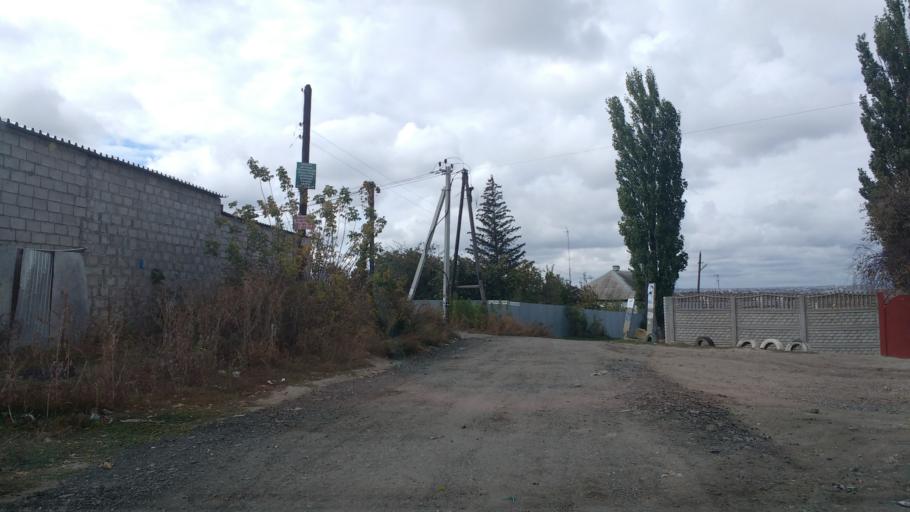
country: RU
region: Volgograd
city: Vodstroy
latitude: 48.7778
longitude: 44.5423
